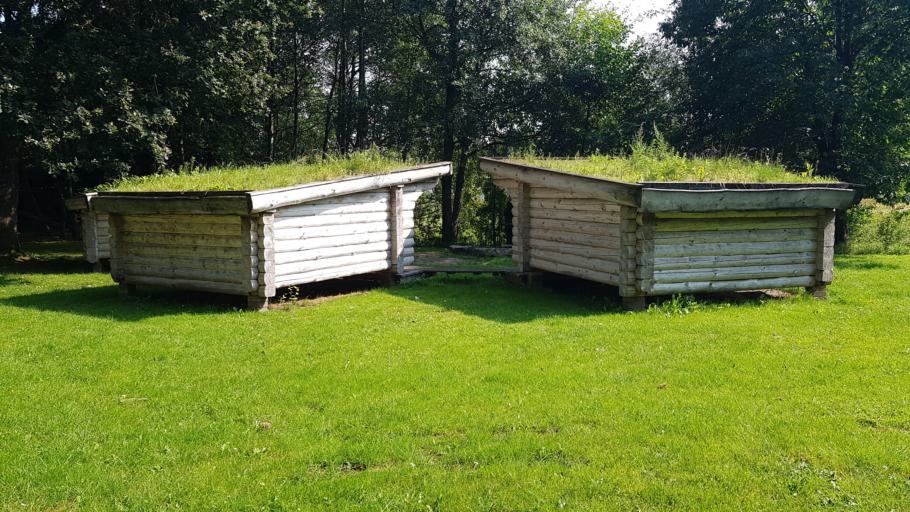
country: DK
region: South Denmark
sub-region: Aabenraa Kommune
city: Rodekro
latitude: 55.0770
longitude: 9.2096
